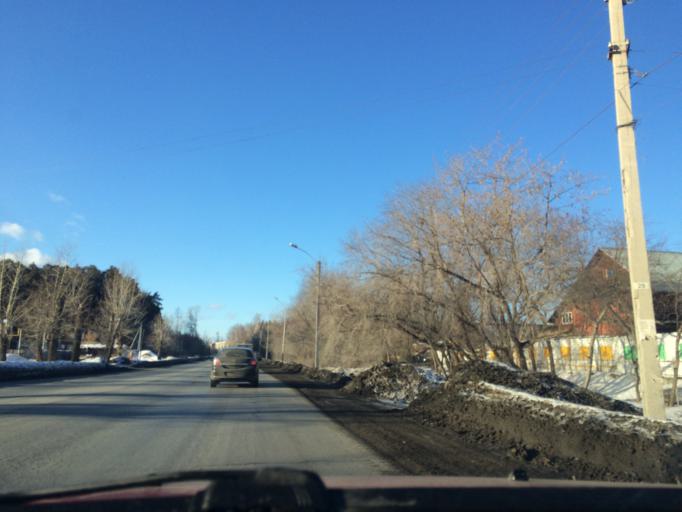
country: RU
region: Sverdlovsk
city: Istok
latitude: 56.7746
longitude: 60.8055
